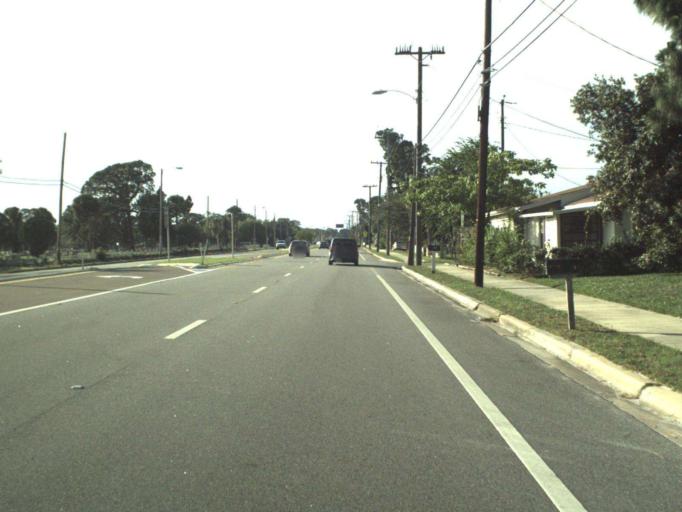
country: US
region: Florida
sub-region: Volusia County
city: Edgewater
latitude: 28.9846
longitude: -80.9033
